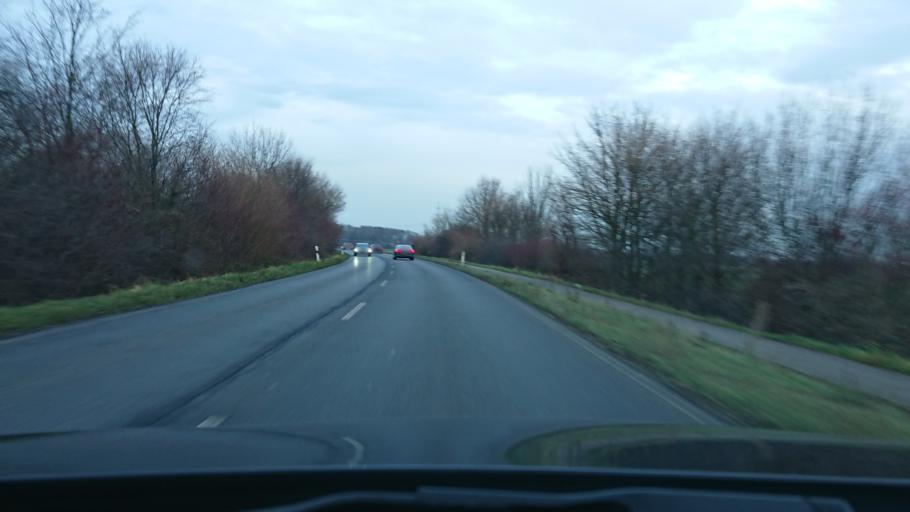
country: DE
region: North Rhine-Westphalia
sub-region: Regierungsbezirk Koln
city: Sinnersdorf
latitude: 51.0333
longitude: 6.8303
